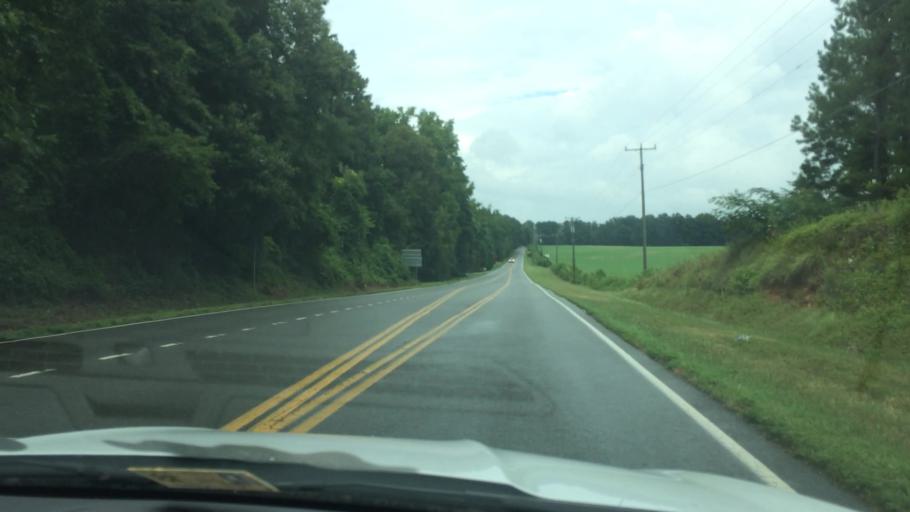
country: US
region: Virginia
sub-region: Charles City County
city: Charles City
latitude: 37.4142
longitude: -77.0442
